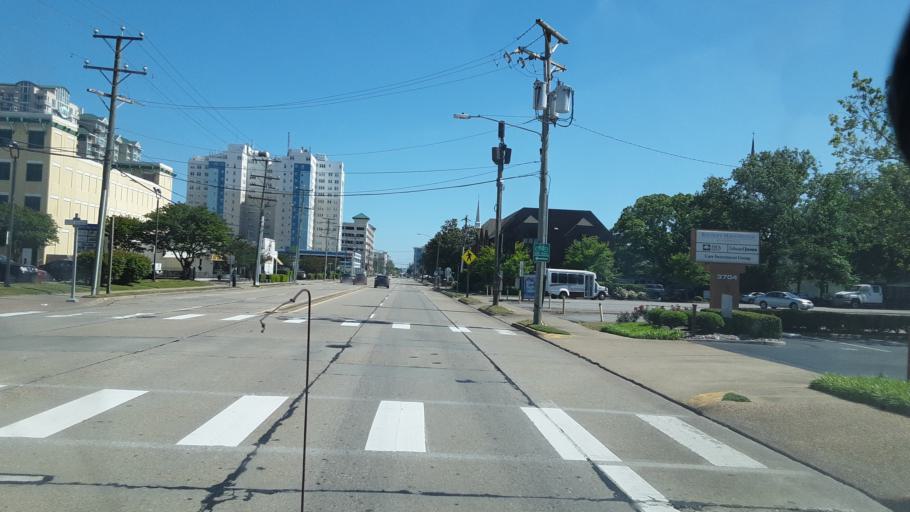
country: US
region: Virginia
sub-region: City of Virginia Beach
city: Virginia Beach
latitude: 36.8650
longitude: -75.9810
